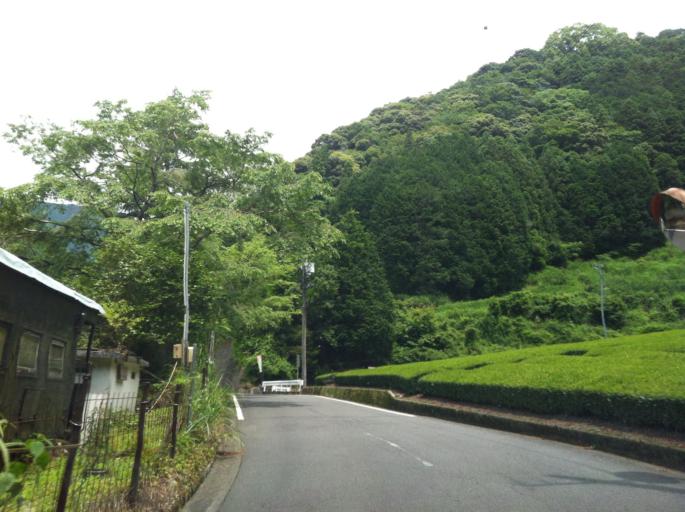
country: JP
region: Shizuoka
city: Shizuoka-shi
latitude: 34.9949
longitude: 138.2905
